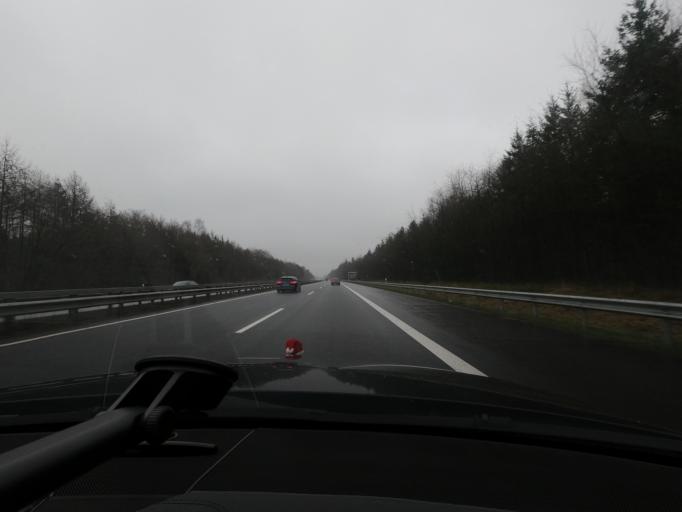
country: DE
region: Schleswig-Holstein
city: Gross Vollstedt
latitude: 54.2338
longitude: 9.8301
